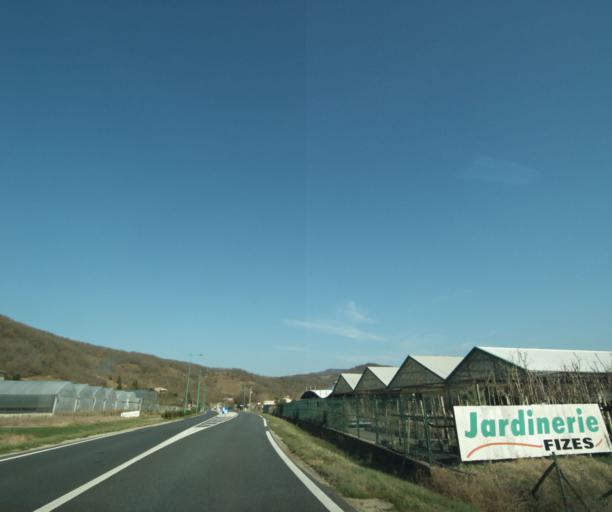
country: FR
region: Midi-Pyrenees
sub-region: Departement de l'Aveyron
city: Saint-Affrique
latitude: 43.9378
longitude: 2.8286
